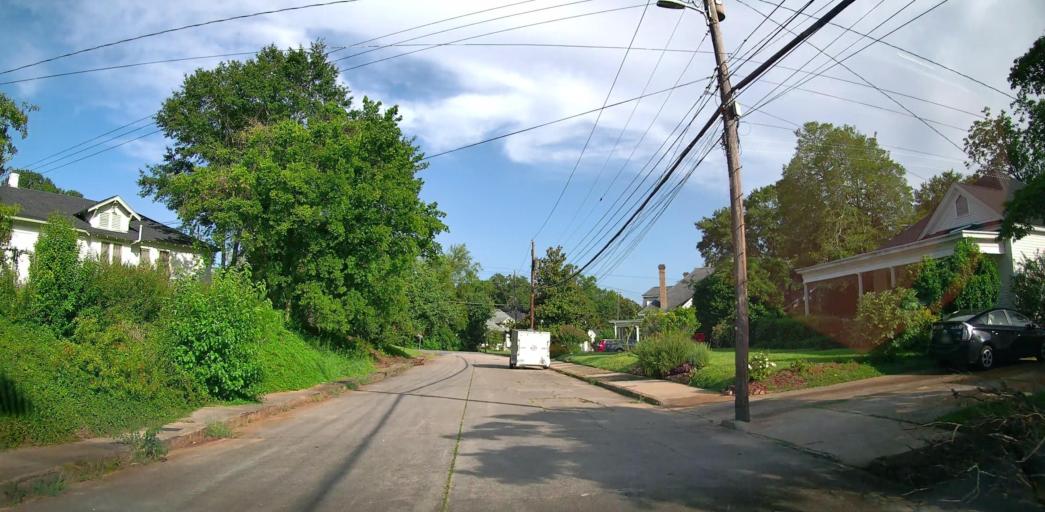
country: US
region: Georgia
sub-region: Bibb County
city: Macon
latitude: 32.8536
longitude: -83.6238
